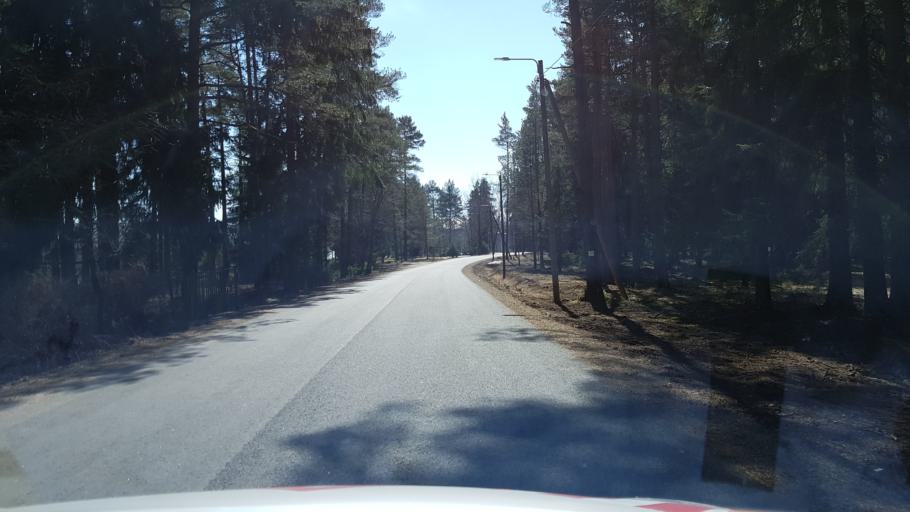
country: EE
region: Ida-Virumaa
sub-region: Kohtla-Nomme vald
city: Kohtla-Nomme
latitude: 59.3602
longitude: 27.1883
